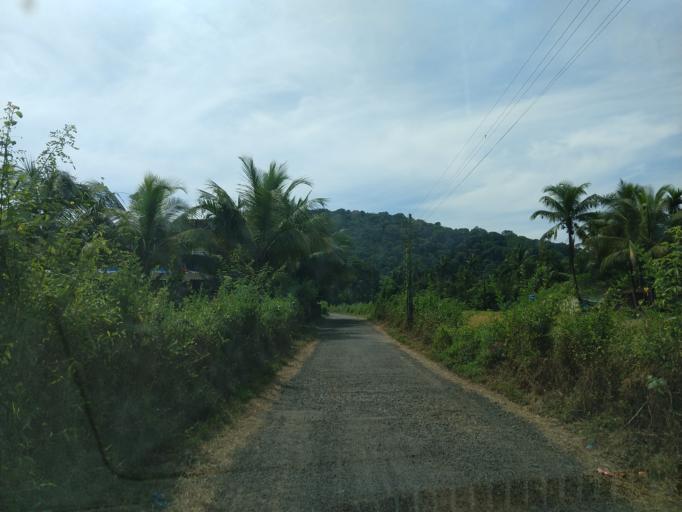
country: IN
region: Maharashtra
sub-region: Sindhudurg
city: Savantvadi
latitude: 15.9757
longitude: 73.7869
